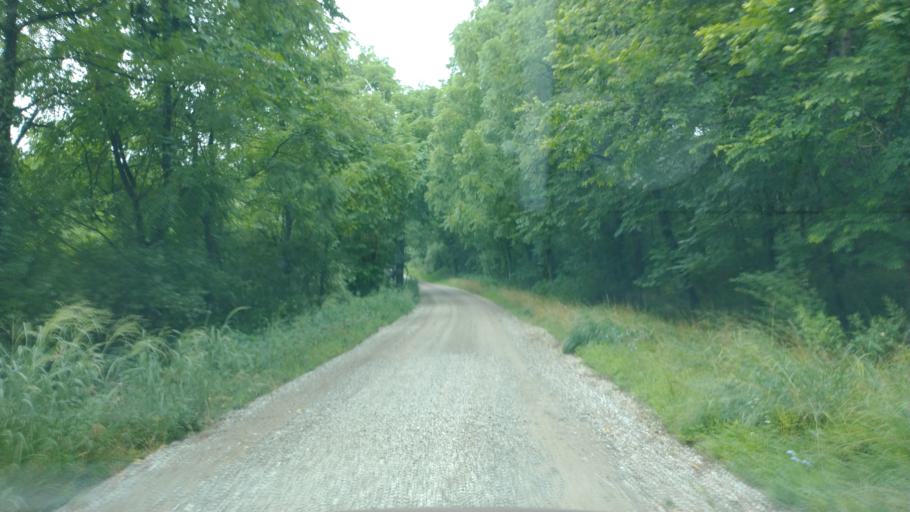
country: US
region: Ohio
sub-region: Meigs County
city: Middleport
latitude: 38.9285
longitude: -82.0627
